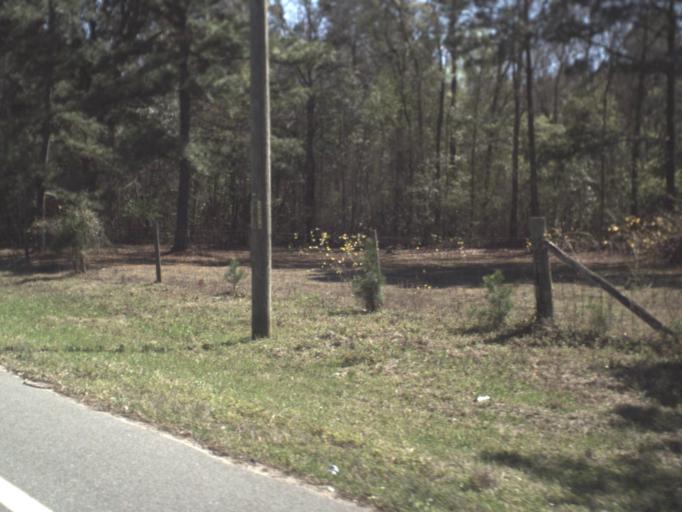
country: US
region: Florida
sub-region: Gadsden County
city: Gretna
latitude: 30.6542
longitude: -84.6870
